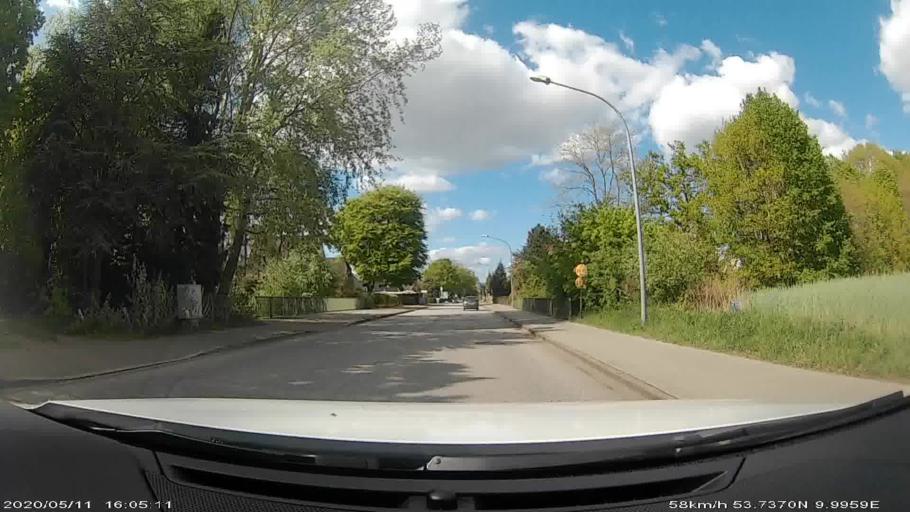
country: DE
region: Schleswig-Holstein
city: Henstedt-Ulzburg
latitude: 53.7472
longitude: 9.9921
